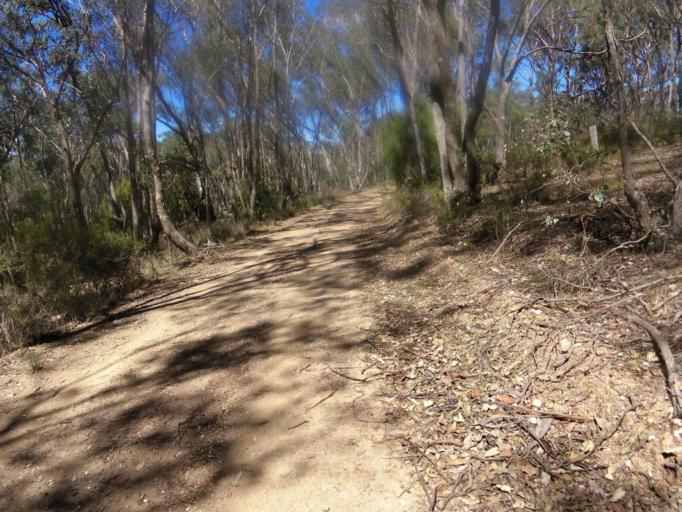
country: AU
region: Victoria
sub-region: Mount Alexander
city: Castlemaine
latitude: -37.0576
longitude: 144.1903
